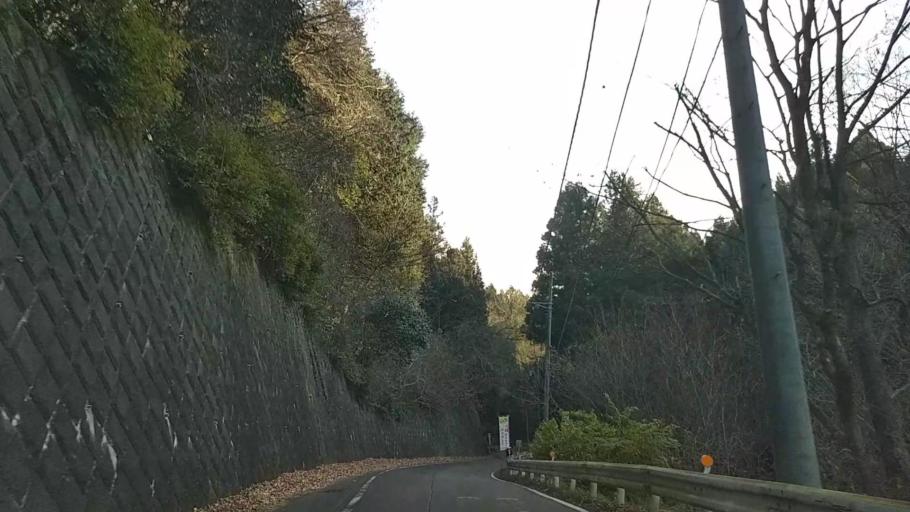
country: JP
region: Yamanashi
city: Uenohara
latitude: 35.5567
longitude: 139.2100
